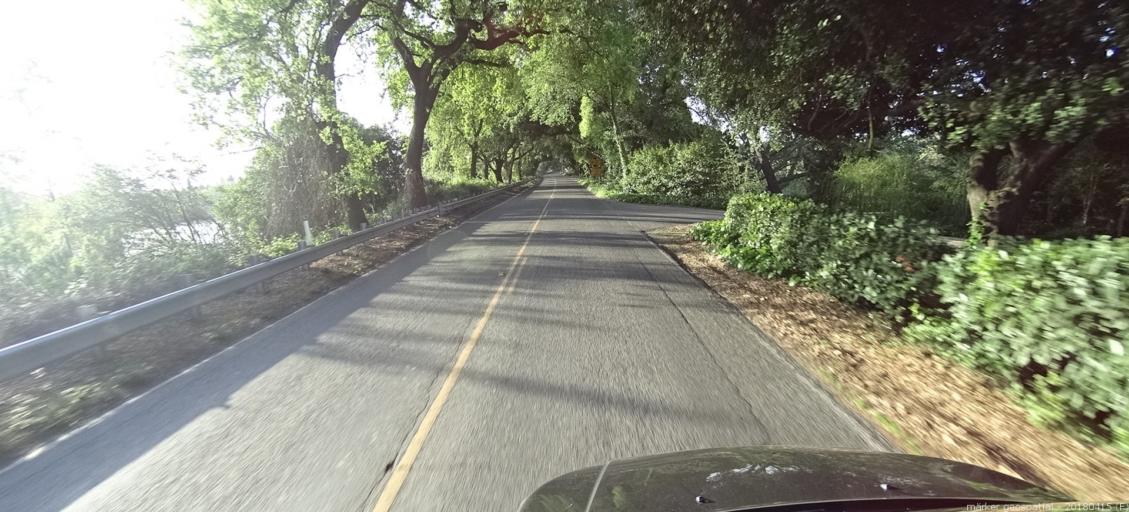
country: US
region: California
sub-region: Sacramento County
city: Walnut Grove
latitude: 38.3091
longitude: -121.5770
